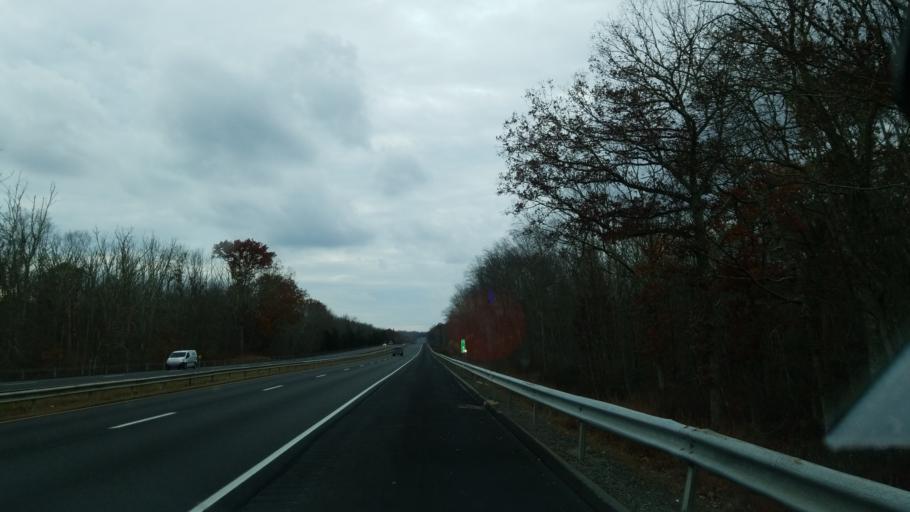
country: US
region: Connecticut
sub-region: New London County
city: Oxoboxo River
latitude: 41.4242
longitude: -72.1282
